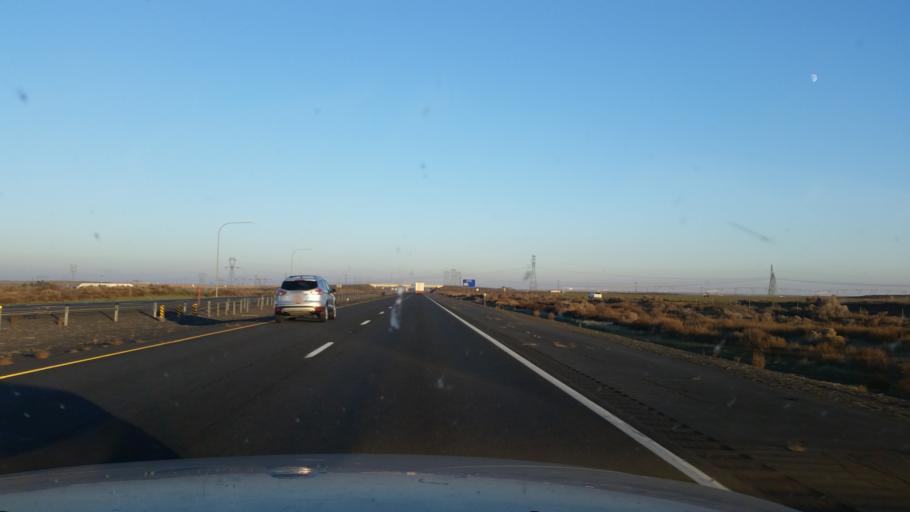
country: US
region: Washington
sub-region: Grant County
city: Royal City
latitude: 47.1042
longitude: -119.5675
